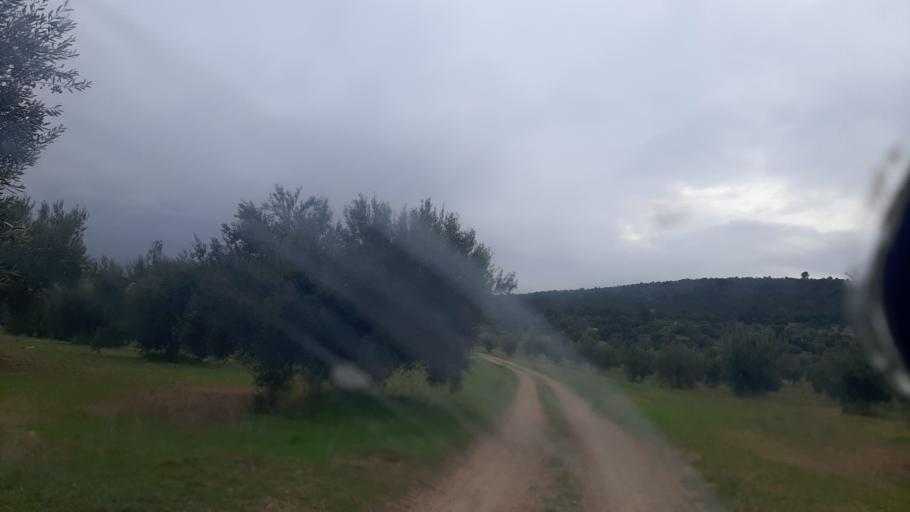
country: TN
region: Tunis
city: La Sebala du Mornag
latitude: 36.5806
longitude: 10.2899
